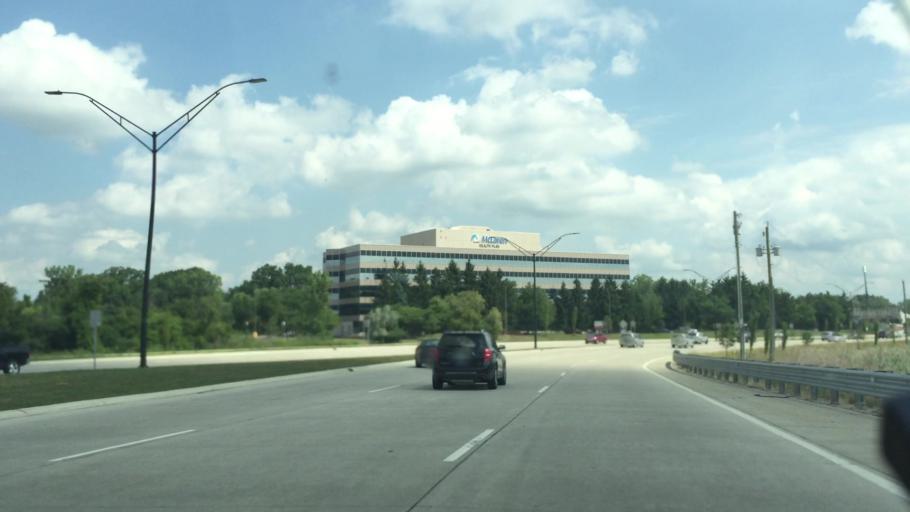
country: US
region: Michigan
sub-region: Oakland County
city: Auburn Hills
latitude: 42.6673
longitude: -83.2389
